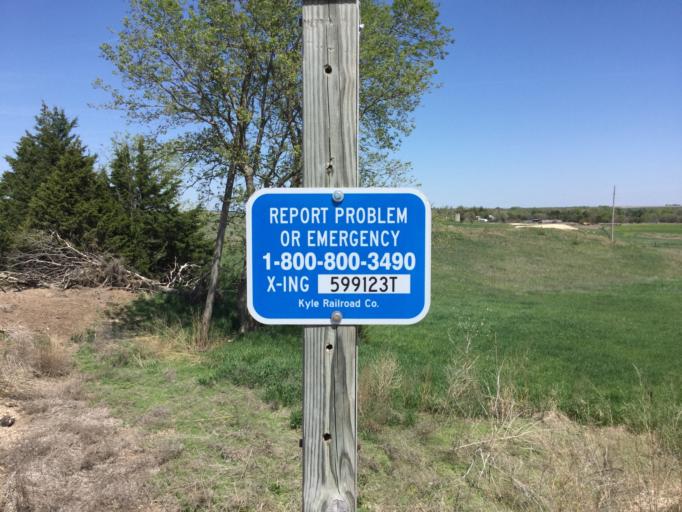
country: US
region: Kansas
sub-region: Smith County
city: Smith Center
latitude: 39.7564
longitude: -98.8769
